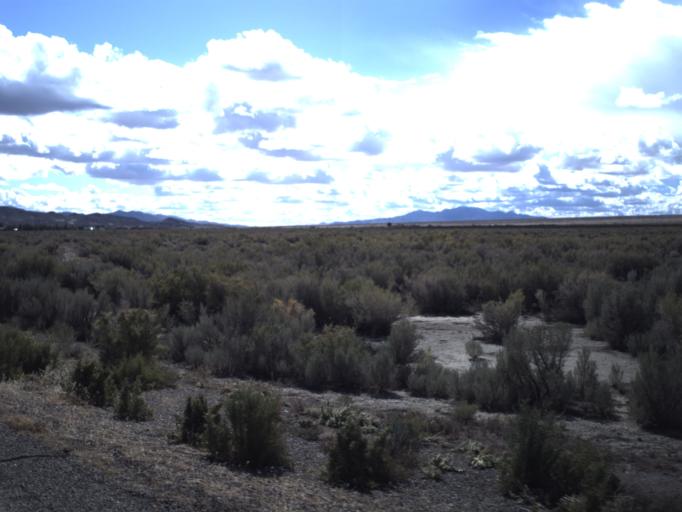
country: US
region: Nevada
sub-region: White Pine County
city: McGill
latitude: 38.9484
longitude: -114.0470
